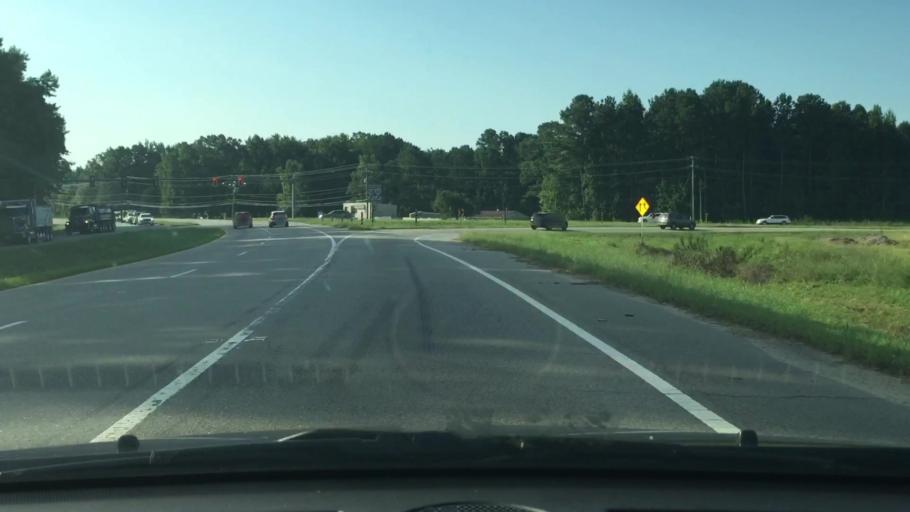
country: US
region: Virginia
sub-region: Isle of Wight County
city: Carrollton
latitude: 36.9419
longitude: -76.5378
